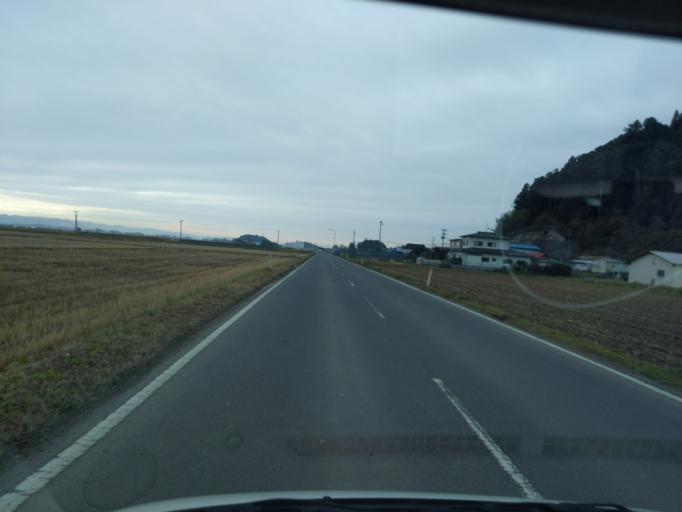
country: JP
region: Iwate
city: Ichinoseki
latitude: 38.7468
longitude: 141.2244
